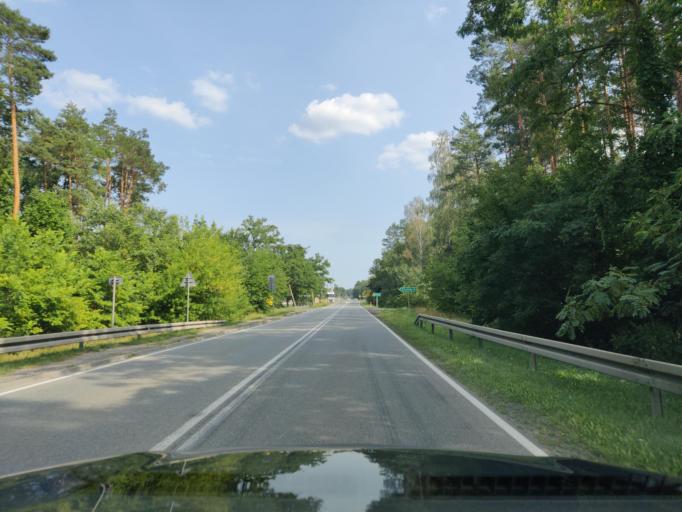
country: PL
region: Masovian Voivodeship
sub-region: Powiat makowski
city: Rozan
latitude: 52.8869
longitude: 21.4183
